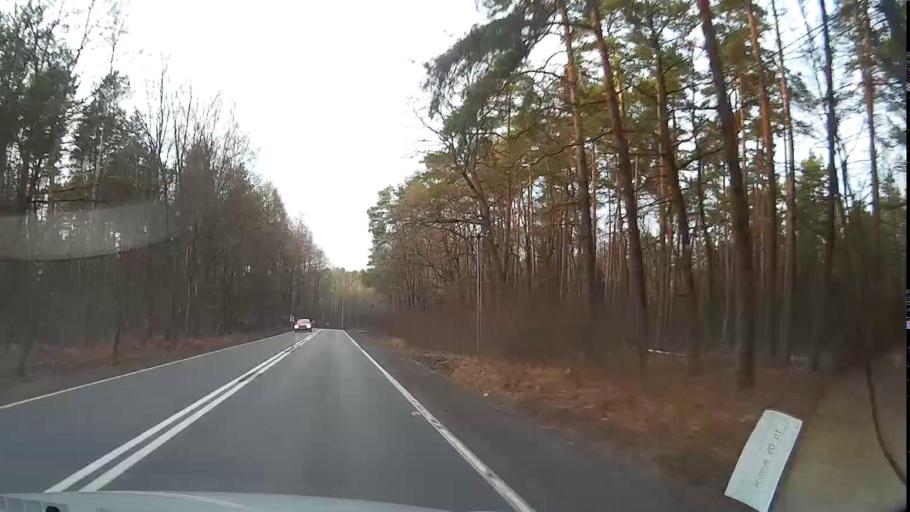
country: PL
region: Lesser Poland Voivodeship
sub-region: Powiat chrzanowski
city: Brodla
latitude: 50.0336
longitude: 19.6090
